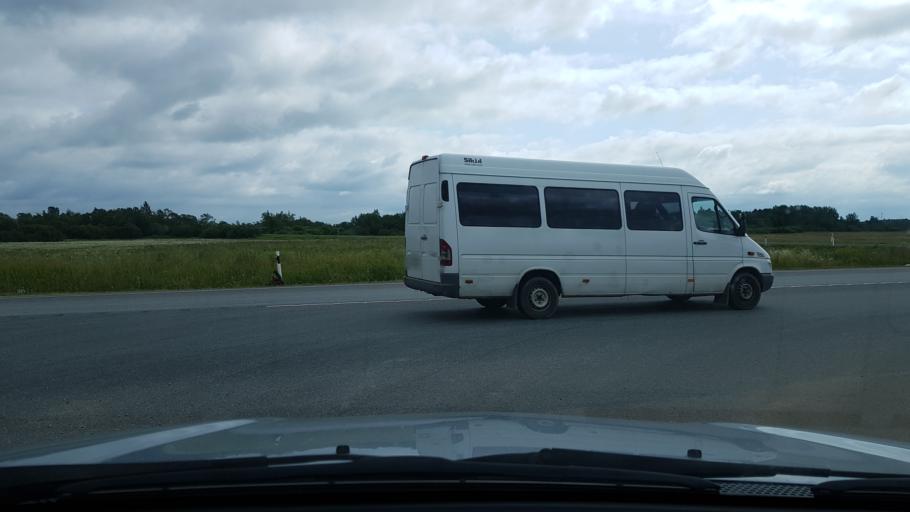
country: EE
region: Ida-Virumaa
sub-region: Narva linn
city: Narva
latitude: 59.3892
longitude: 28.1309
